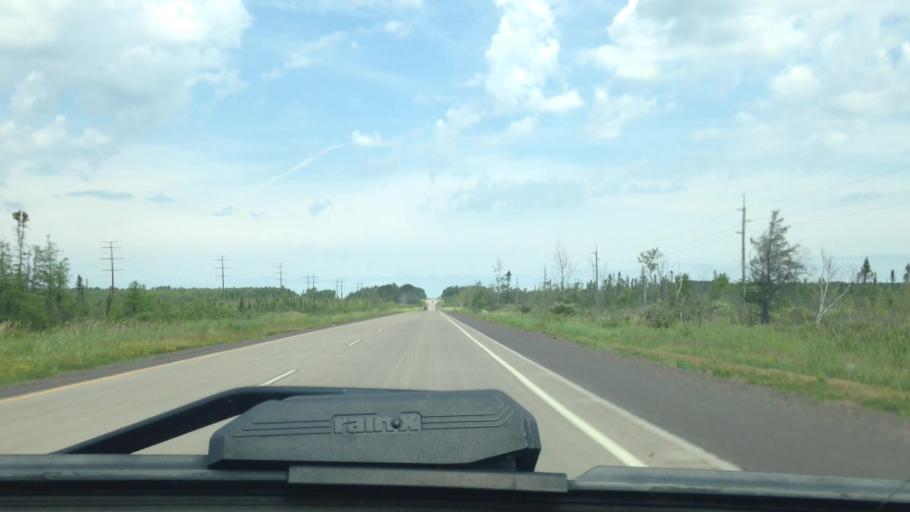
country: US
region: Wisconsin
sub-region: Douglas County
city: Lake Nebagamon
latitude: 46.2626
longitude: -91.8002
